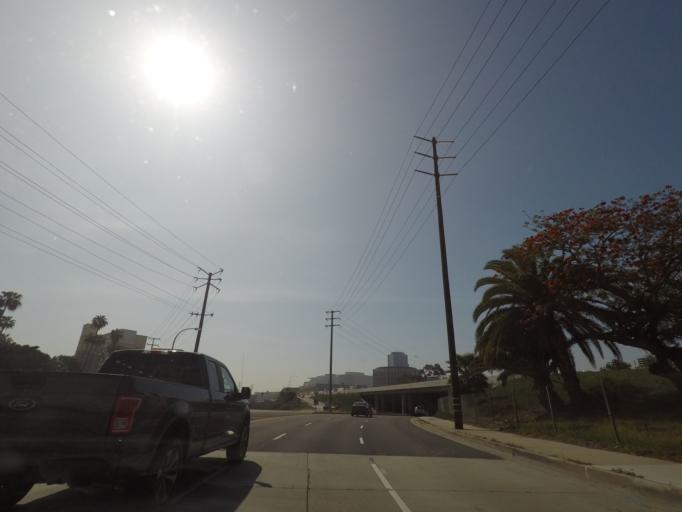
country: US
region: California
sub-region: Los Angeles County
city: Ladera Heights
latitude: 33.9833
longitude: -118.3948
